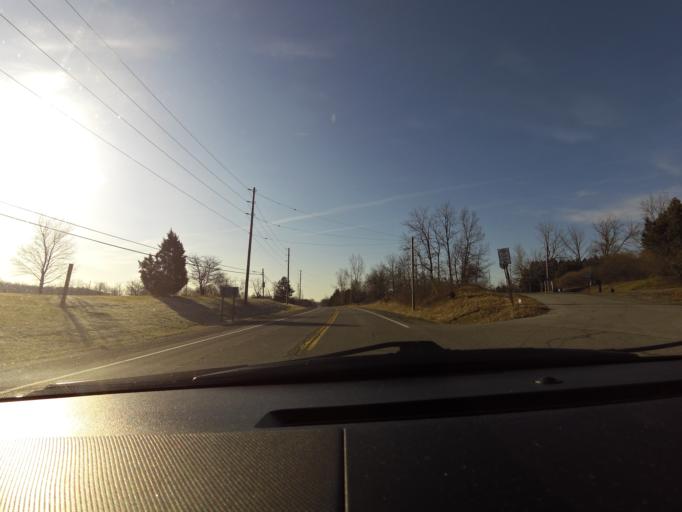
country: CA
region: Ontario
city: Ancaster
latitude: 43.0514
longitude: -79.9122
